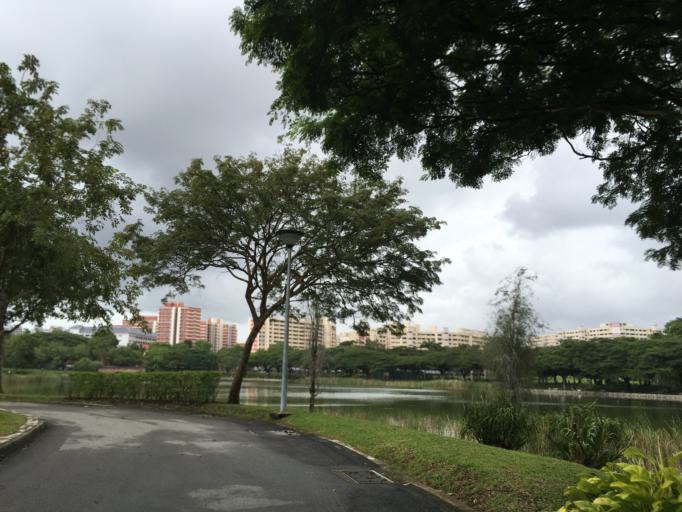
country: MY
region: Johor
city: Kampung Pasir Gudang Baru
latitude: 1.3779
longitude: 103.8993
